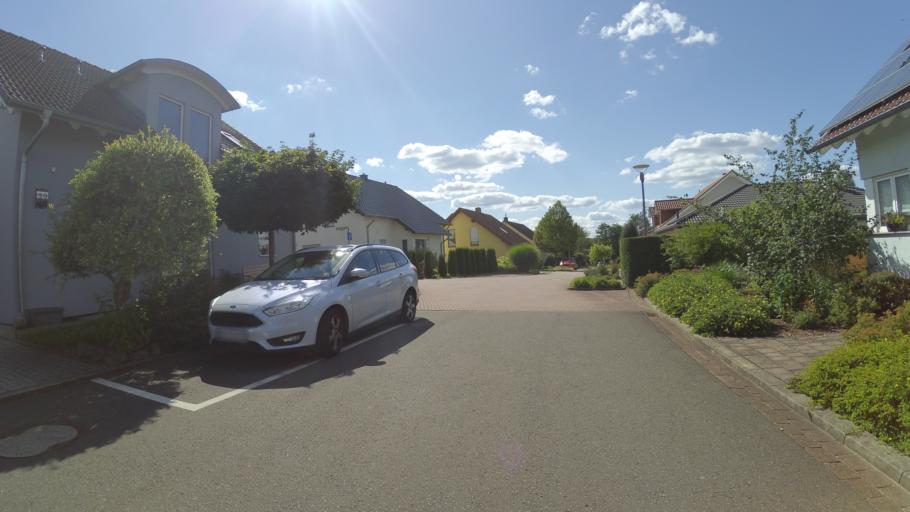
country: DE
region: Saarland
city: Illingen
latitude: 49.3872
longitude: 7.0641
